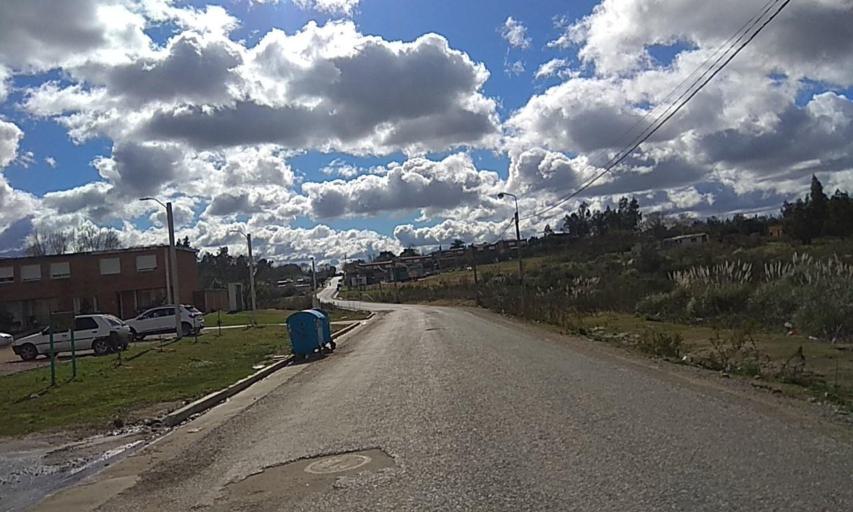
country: UY
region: Florida
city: Florida
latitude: -34.0898
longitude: -56.2264
